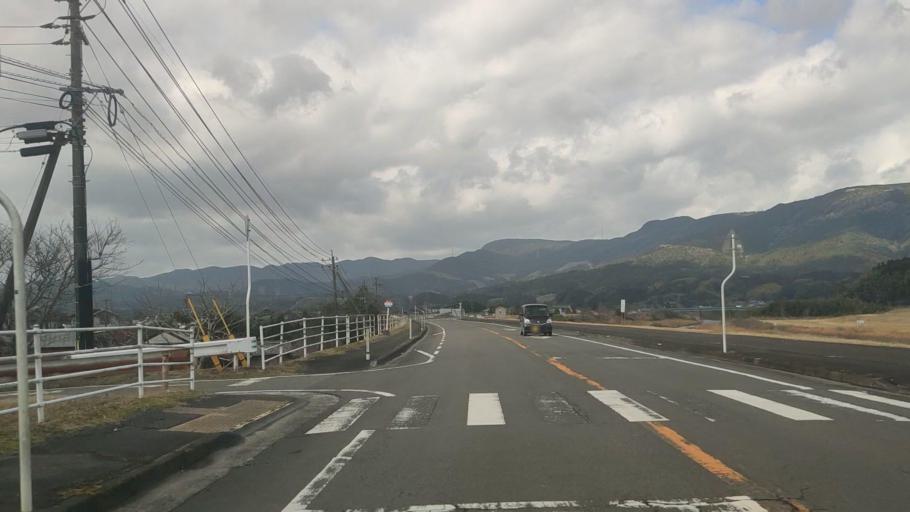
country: JP
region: Kumamoto
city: Hitoyoshi
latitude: 32.0553
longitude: 130.7969
